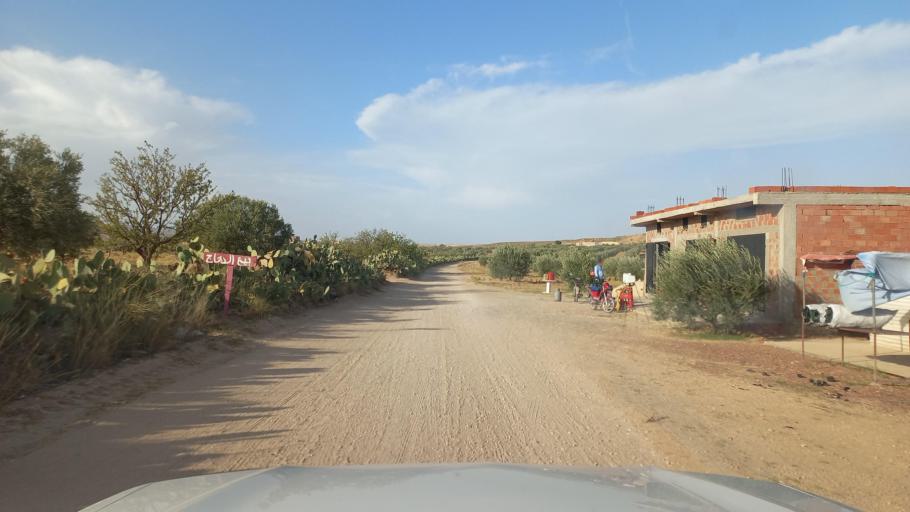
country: TN
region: Al Qasrayn
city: Kasserine
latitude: 35.2427
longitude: 8.9170
